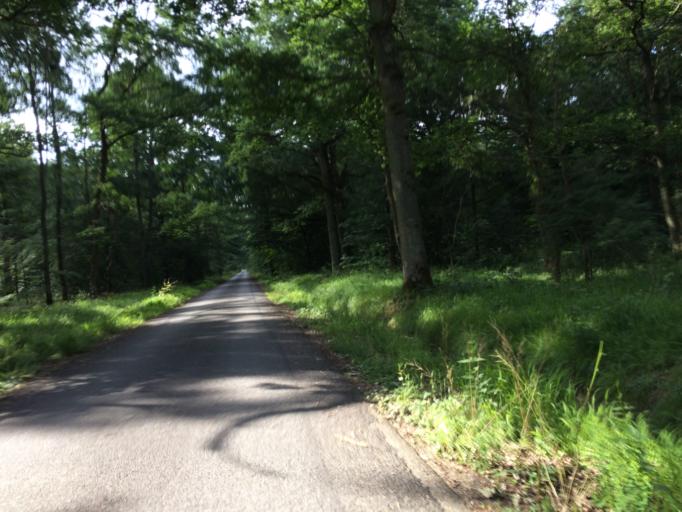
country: FR
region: Ile-de-France
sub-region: Departement de l'Essonne
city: Soisy-sur-Seine
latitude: 48.6600
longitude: 2.4748
